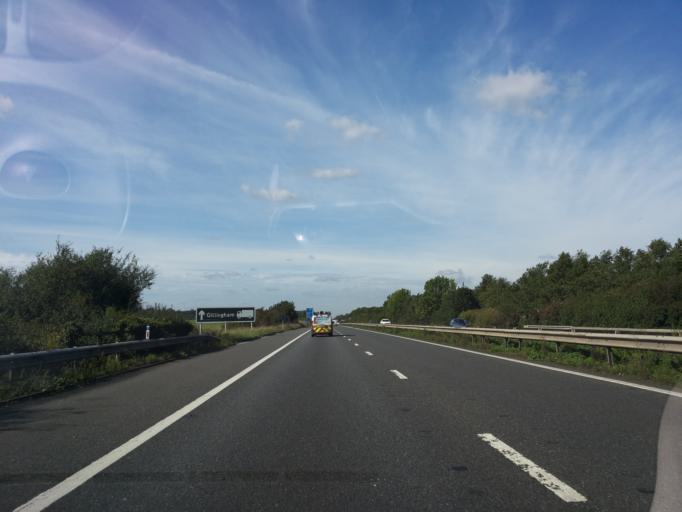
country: GB
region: England
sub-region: Kent
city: Newington
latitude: 51.3244
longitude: 0.6767
